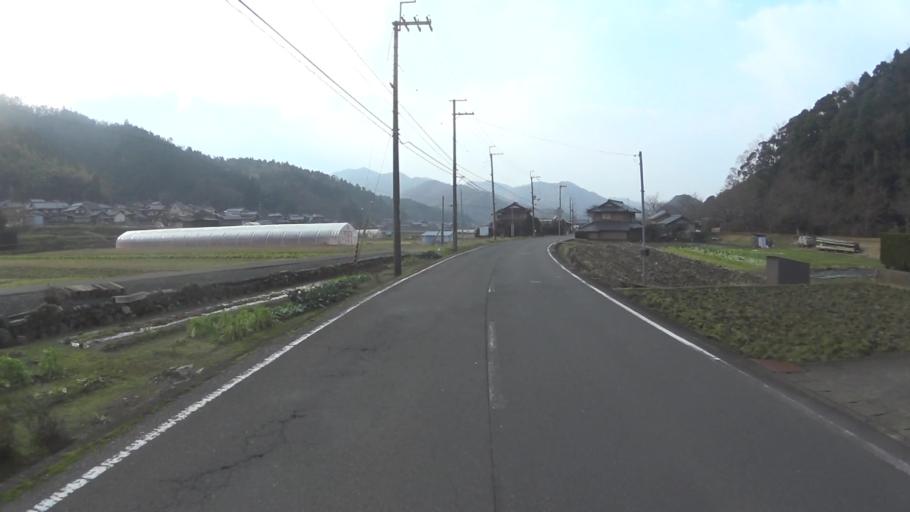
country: JP
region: Kyoto
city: Maizuru
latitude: 35.4460
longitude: 135.4273
